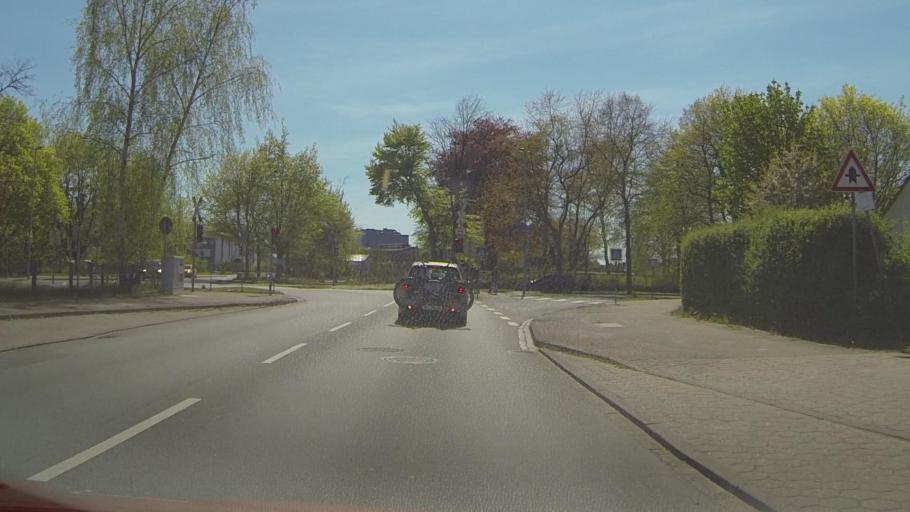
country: DE
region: Schleswig-Holstein
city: Uetersen
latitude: 53.6829
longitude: 9.6826
